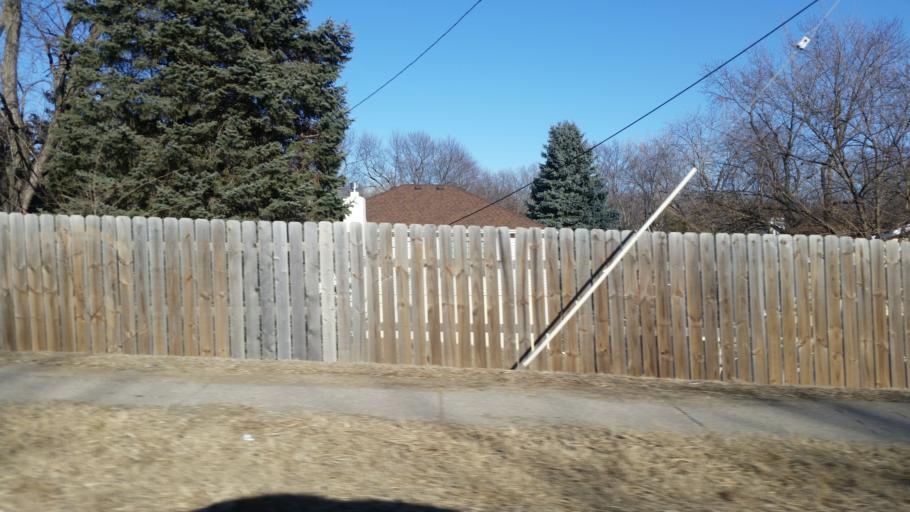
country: US
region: Nebraska
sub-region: Sarpy County
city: Bellevue
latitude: 41.1586
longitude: -95.9201
